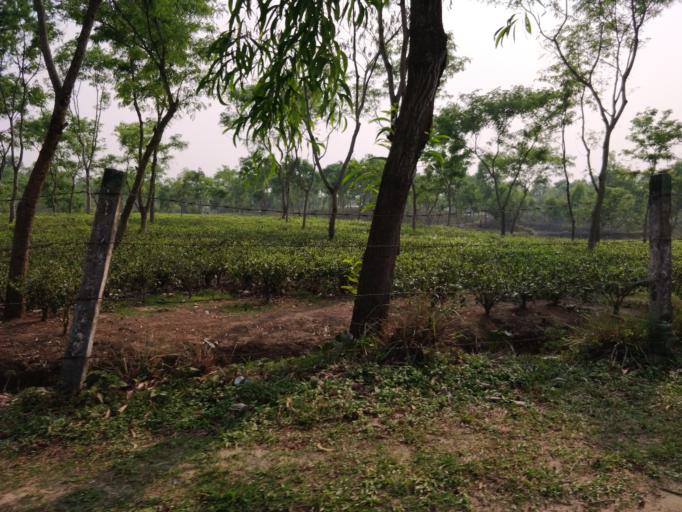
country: IN
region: Tripura
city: Khowai
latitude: 24.1300
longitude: 91.3873
